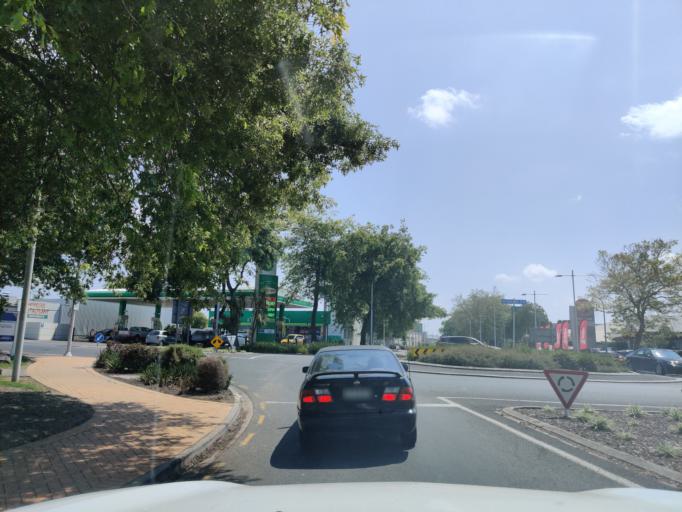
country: NZ
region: Auckland
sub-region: Auckland
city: Pukekohe East
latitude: -37.1991
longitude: 174.9041
